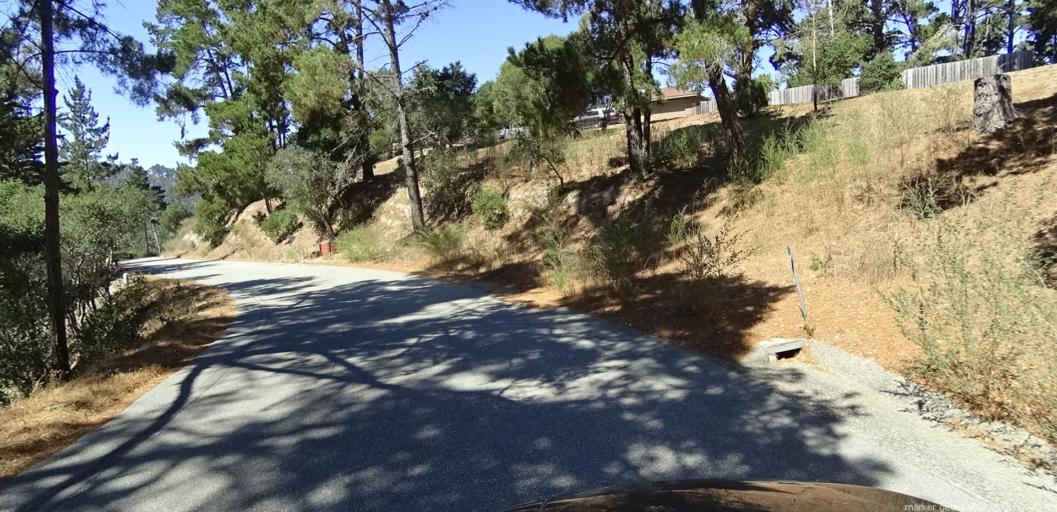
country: US
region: California
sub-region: Monterey County
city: Monterey
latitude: 36.5743
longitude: -121.8887
